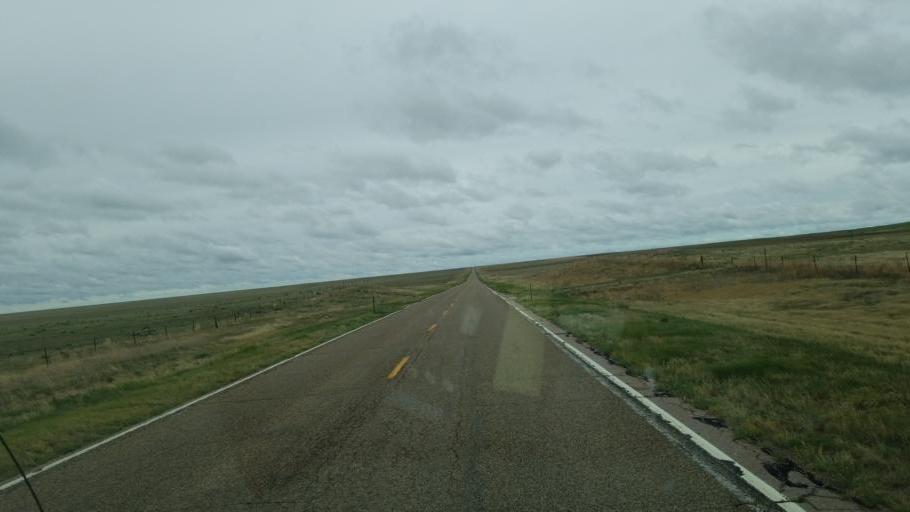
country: US
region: Colorado
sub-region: Lincoln County
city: Hugo
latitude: 38.8500
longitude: -103.4202
